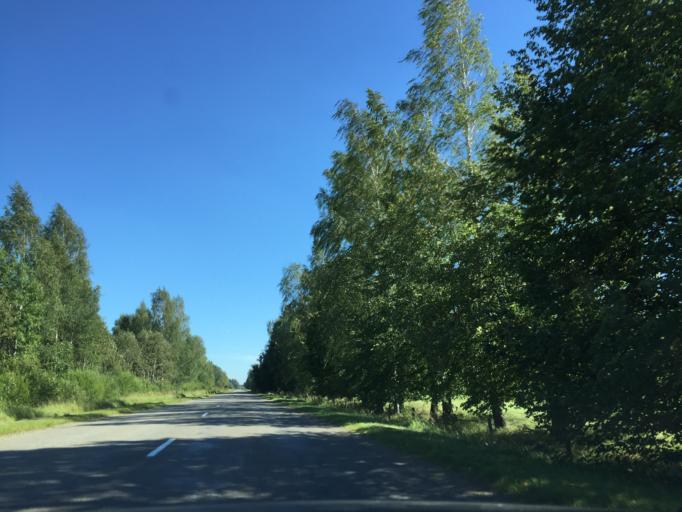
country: LV
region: Akniste
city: Akniste
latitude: 56.1520
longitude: 25.7742
